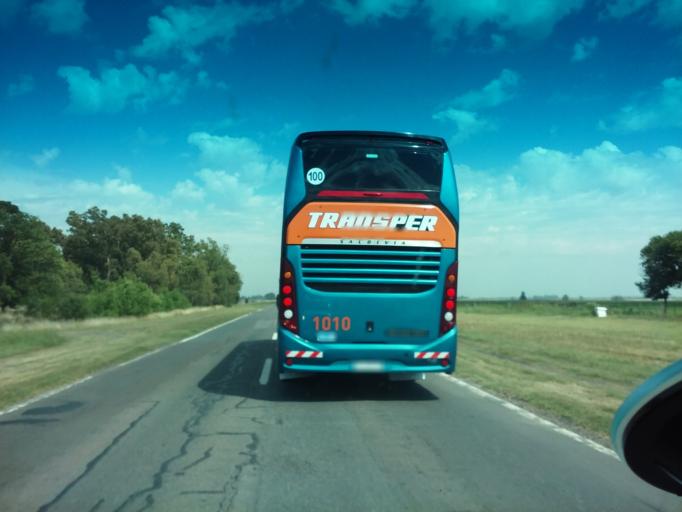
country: AR
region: Buenos Aires
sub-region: Partido de Carlos Casares
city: Carlos Casares
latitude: -35.6494
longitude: -61.3817
